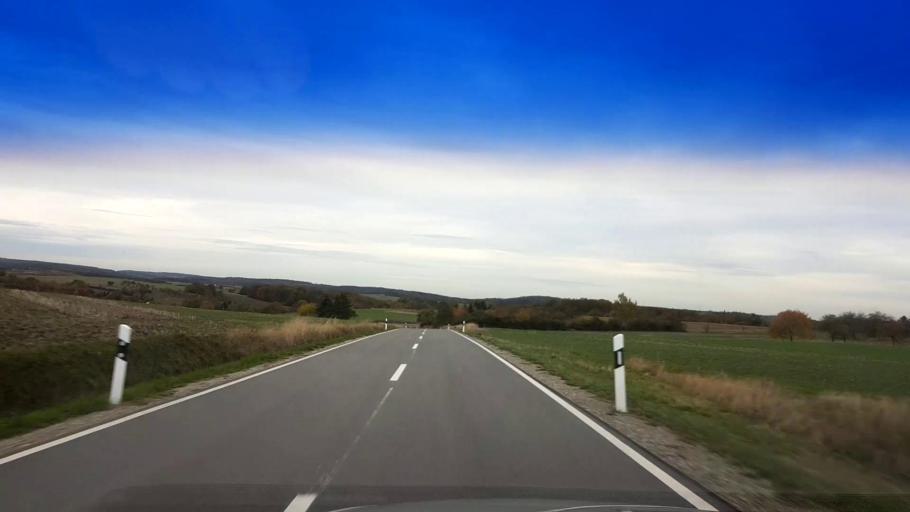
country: DE
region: Bavaria
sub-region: Upper Franconia
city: Priesendorf
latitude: 49.9280
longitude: 10.7048
